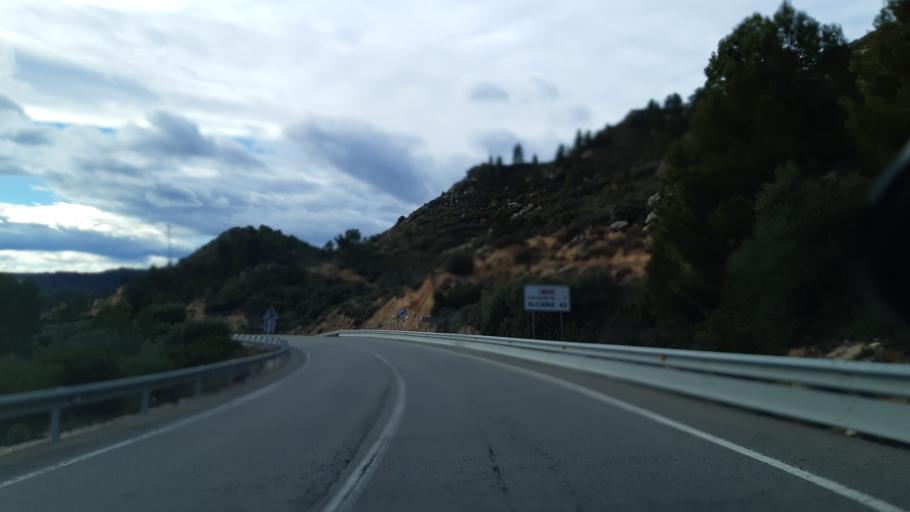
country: ES
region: Catalonia
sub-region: Provincia de Tarragona
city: Caseres
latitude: 41.0455
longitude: 0.2483
